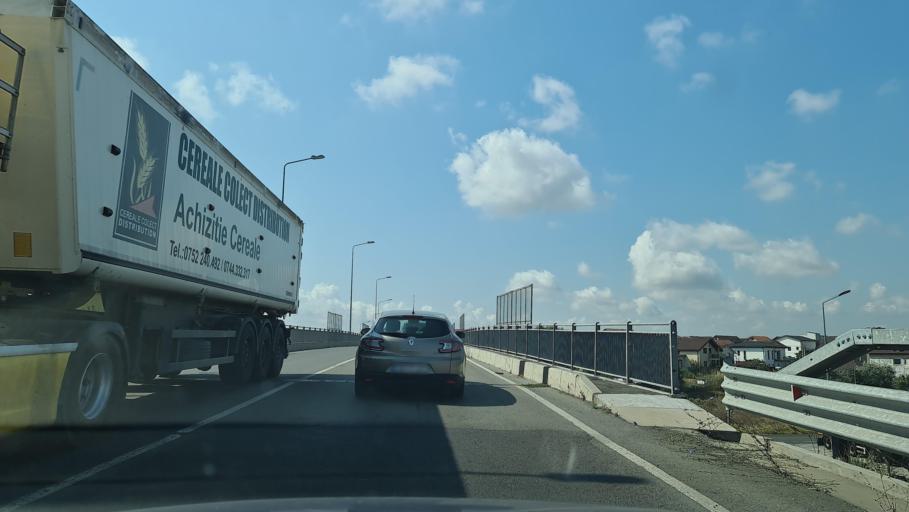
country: RO
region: Constanta
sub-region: Comuna Agigea
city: Agigea
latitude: 44.0961
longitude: 28.6397
